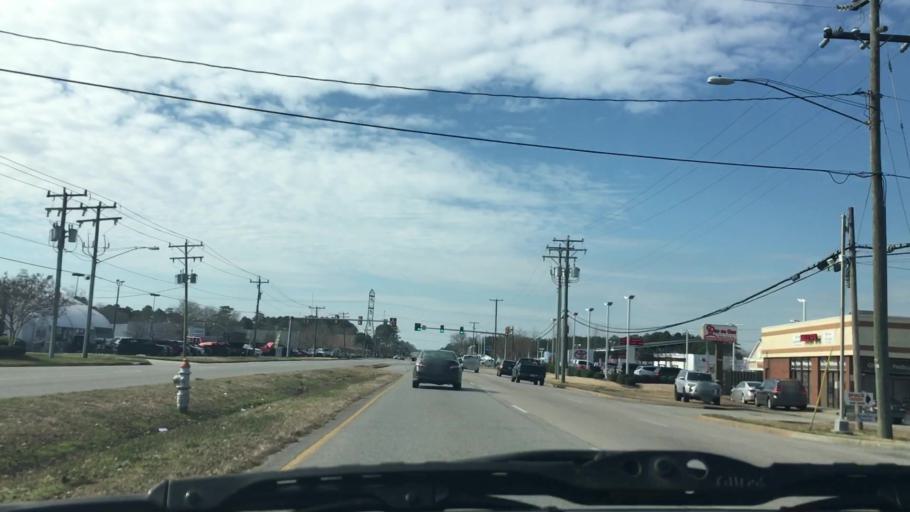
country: US
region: Virginia
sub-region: City of Portsmouth
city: Portsmouth Heights
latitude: 36.8656
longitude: -76.4140
